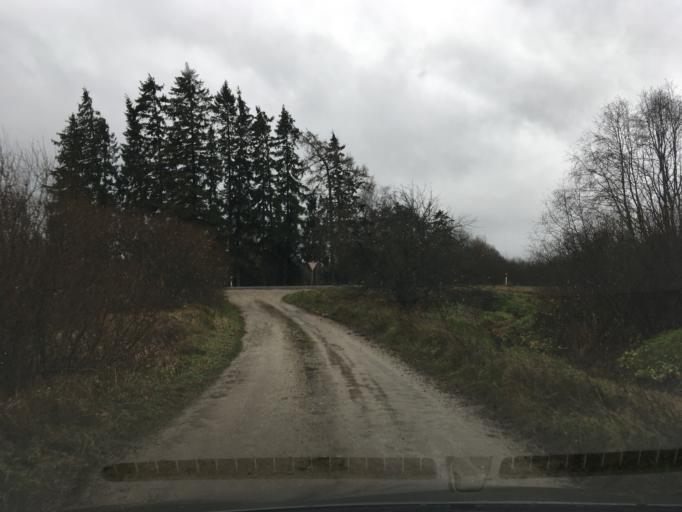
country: EE
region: Laeaene
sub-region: Lihula vald
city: Lihula
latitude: 58.7008
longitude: 23.8565
